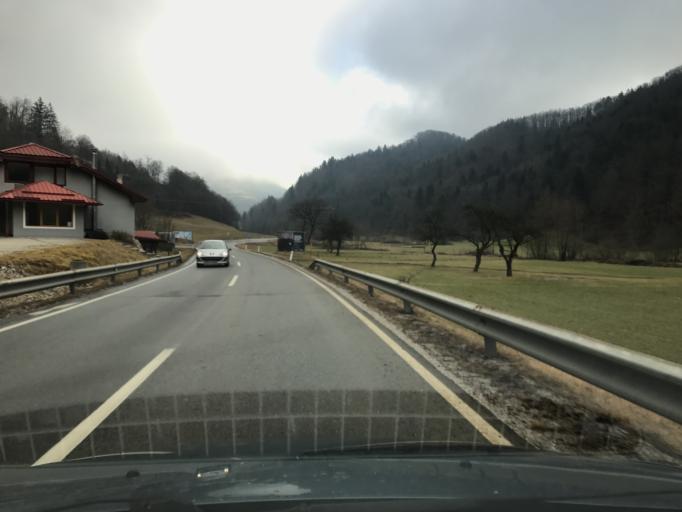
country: SI
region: Vransko
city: Vransko
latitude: 46.2240
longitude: 14.9237
